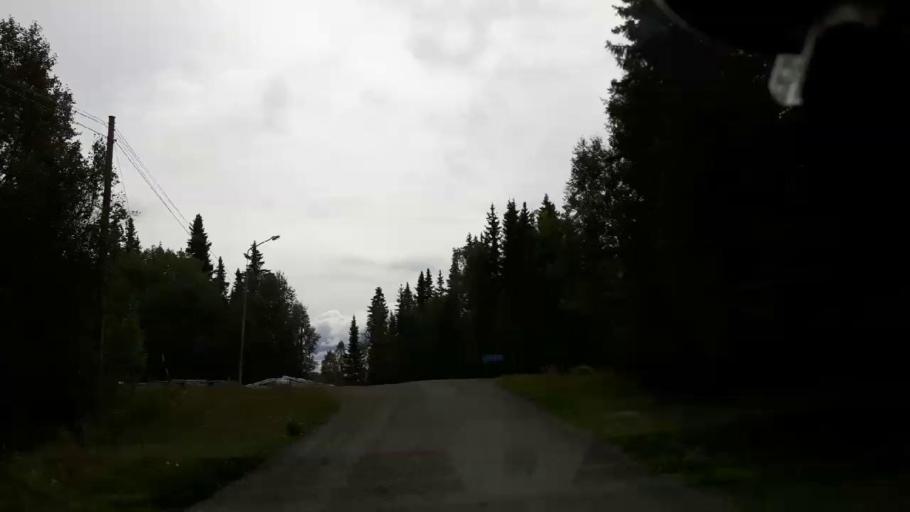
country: SE
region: Jaemtland
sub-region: Krokoms Kommun
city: Valla
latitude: 63.7078
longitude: 13.8645
